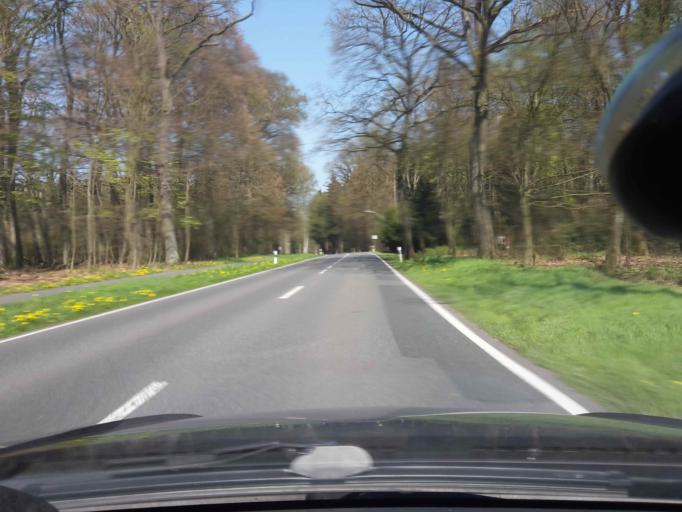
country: DE
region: Lower Saxony
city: Schneverdingen
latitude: 53.0905
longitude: 9.8466
